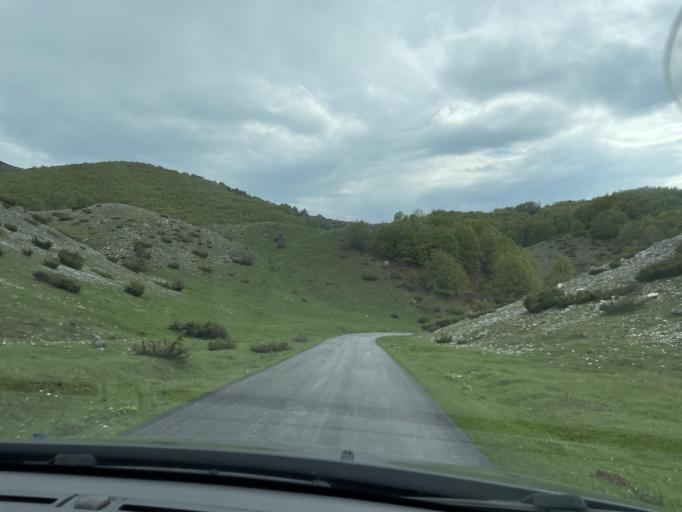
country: MK
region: Opstina Rostusa
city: Rostusha
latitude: 41.6018
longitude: 20.6837
